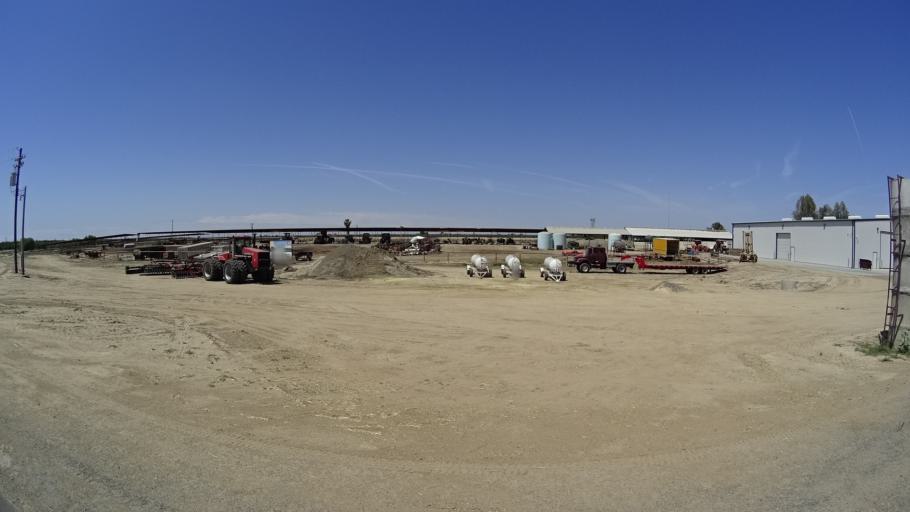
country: US
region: California
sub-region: Kings County
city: Armona
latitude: 36.2527
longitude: -119.7089
